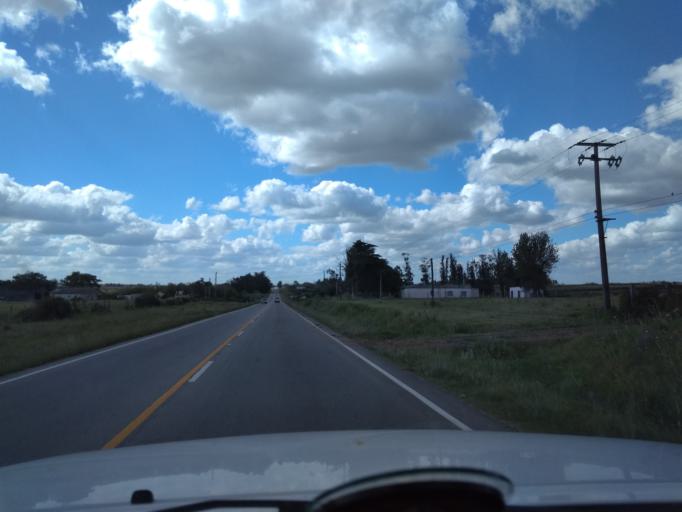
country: UY
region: Canelones
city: Joaquin Suarez
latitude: -34.7016
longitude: -56.0572
